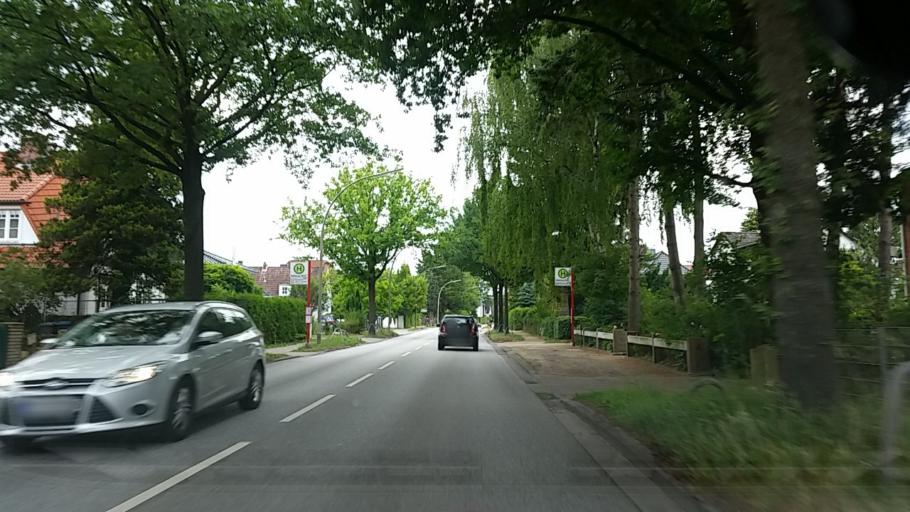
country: DE
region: Schleswig-Holstein
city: Bonningstedt
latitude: 53.6390
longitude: 9.9241
